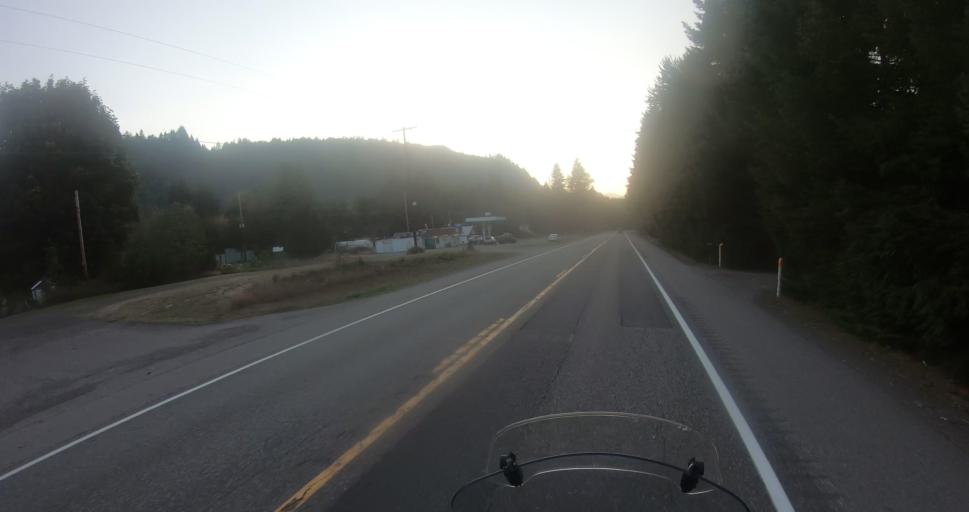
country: US
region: Washington
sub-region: Lewis County
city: Morton
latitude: 46.5396
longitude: -122.0357
